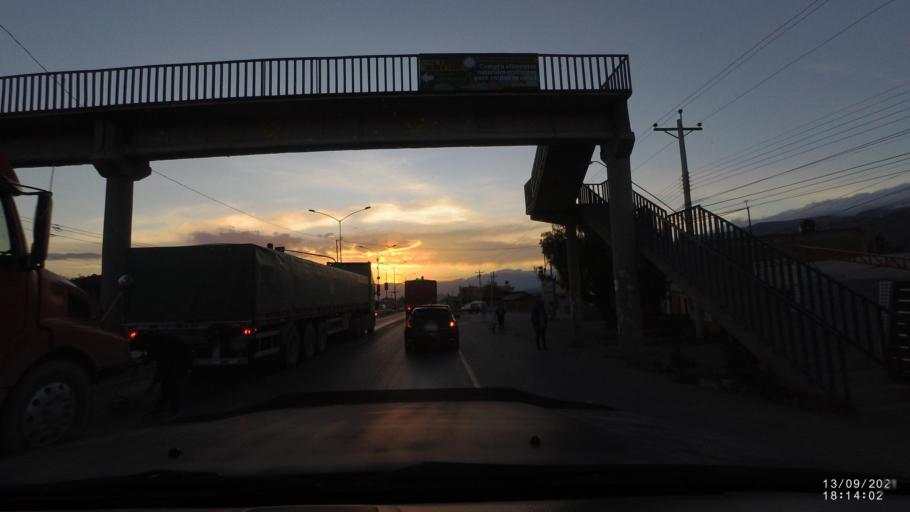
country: BO
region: Cochabamba
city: Cochabamba
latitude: -17.4051
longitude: -66.0154
